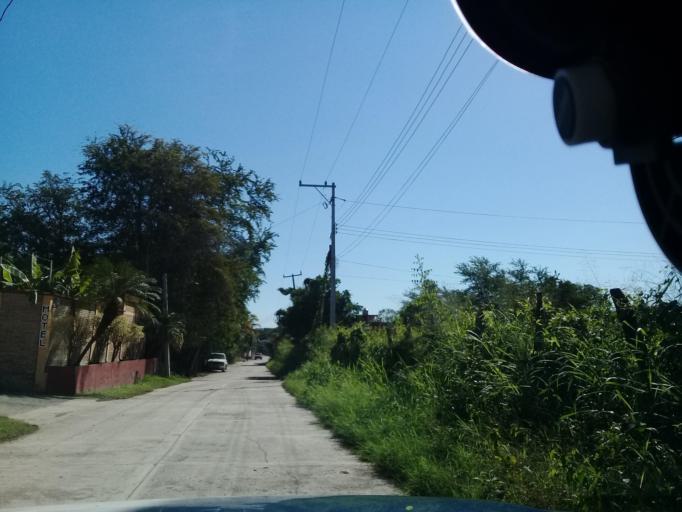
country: MX
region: Hidalgo
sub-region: Huejutla de Reyes
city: Parque de Poblamiento Solidaridad
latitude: 21.1600
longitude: -98.4061
